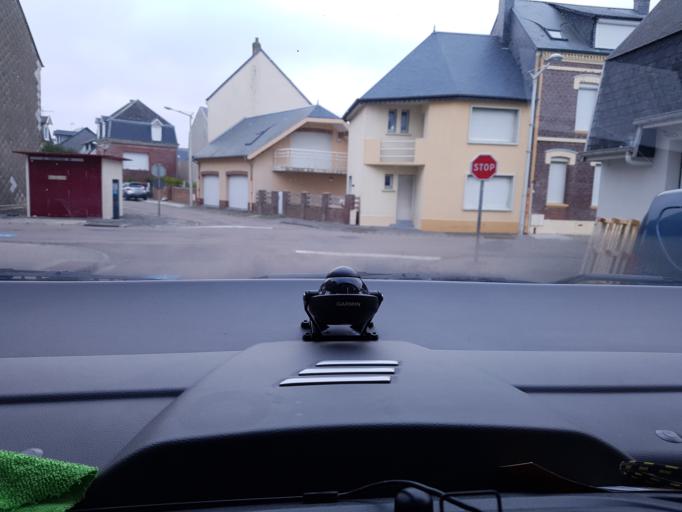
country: FR
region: Picardie
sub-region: Departement de la Somme
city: Cayeux-sur-Mer
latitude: 50.1808
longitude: 1.4909
